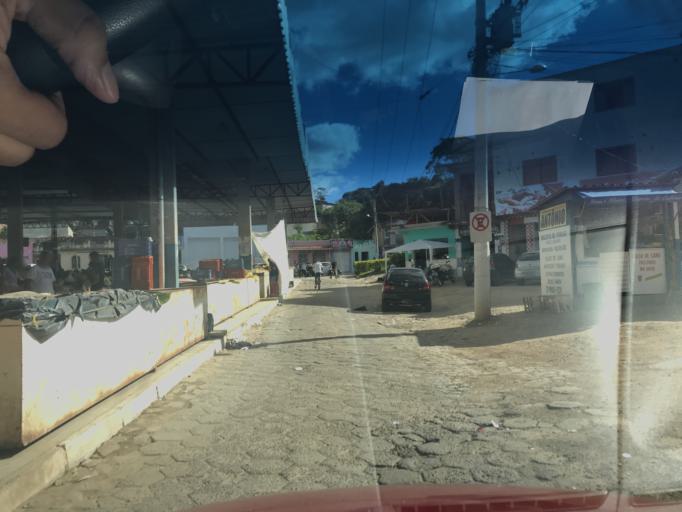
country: BR
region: Bahia
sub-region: Gandu
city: Gandu
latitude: -13.7436
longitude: -39.4902
